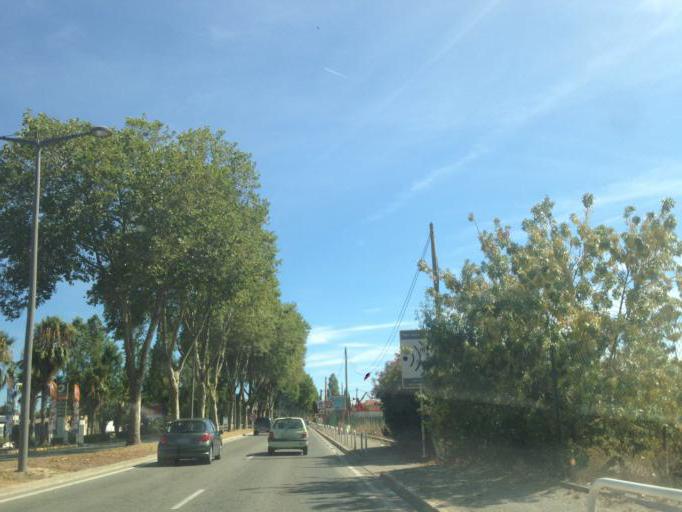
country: FR
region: Provence-Alpes-Cote d'Azur
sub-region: Departement des Alpes-Maritimes
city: Saint-Laurent-du-Var
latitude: 43.6879
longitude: 7.1968
